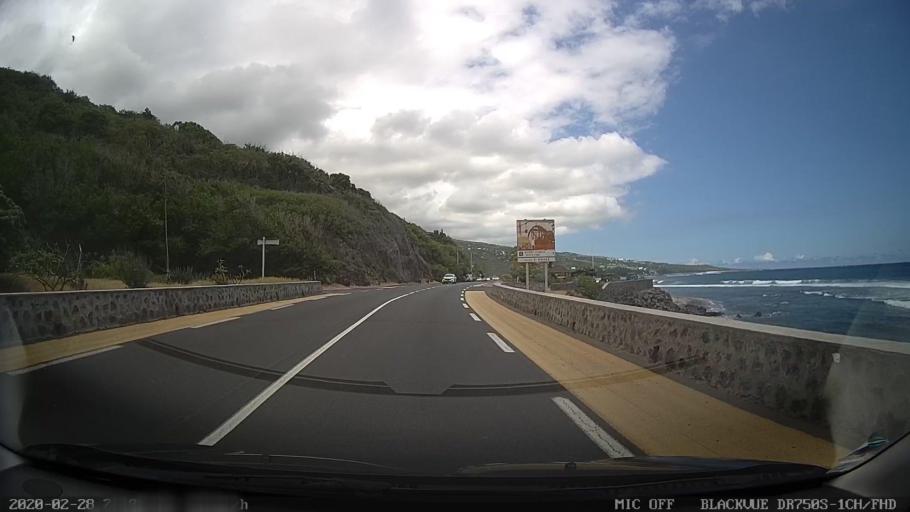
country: RE
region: Reunion
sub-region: Reunion
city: Saint-Leu
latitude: -21.1540
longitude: 55.2822
